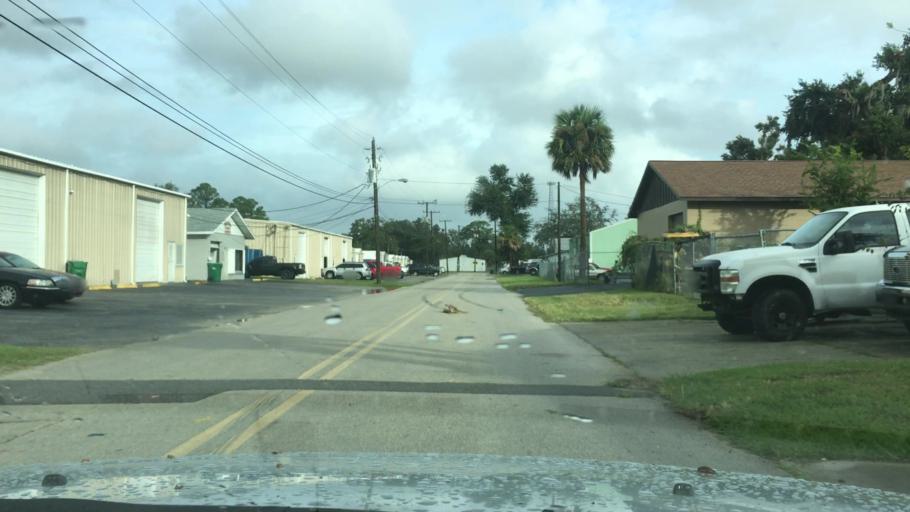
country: US
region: Florida
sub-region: Volusia County
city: Holly Hill
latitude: 29.2400
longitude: -81.0409
